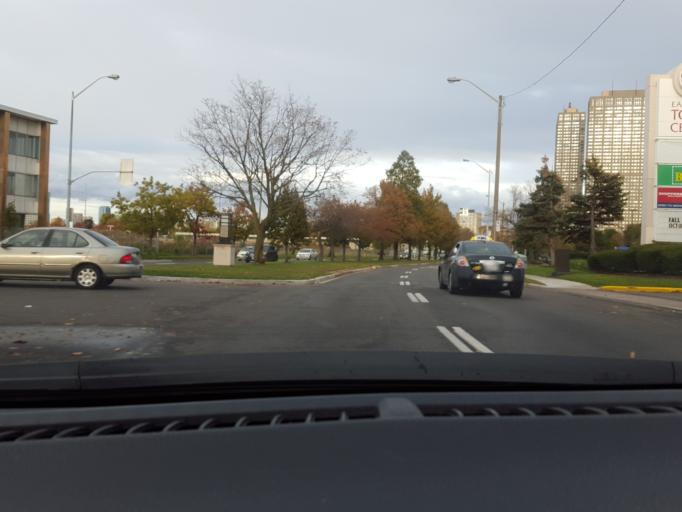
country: CA
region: Ontario
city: Toronto
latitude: 43.7063
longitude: -79.3485
